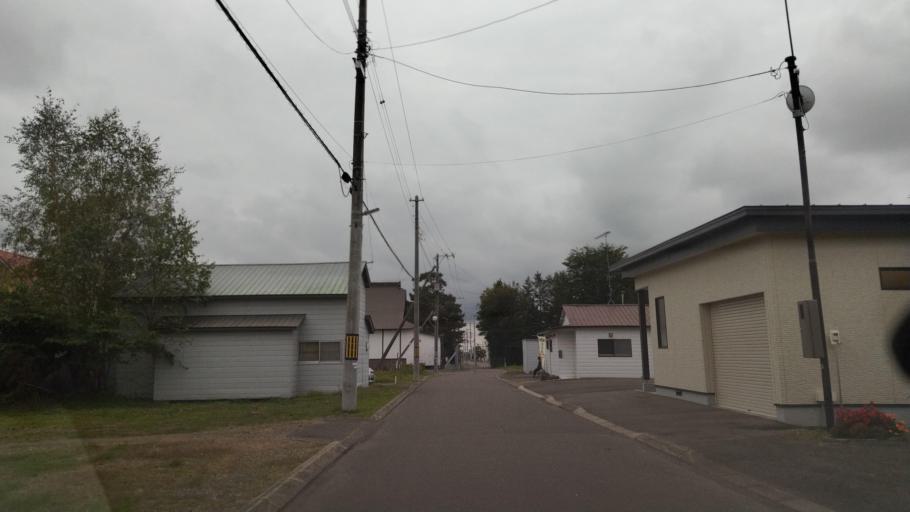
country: JP
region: Hokkaido
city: Otofuke
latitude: 43.2366
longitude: 143.2930
